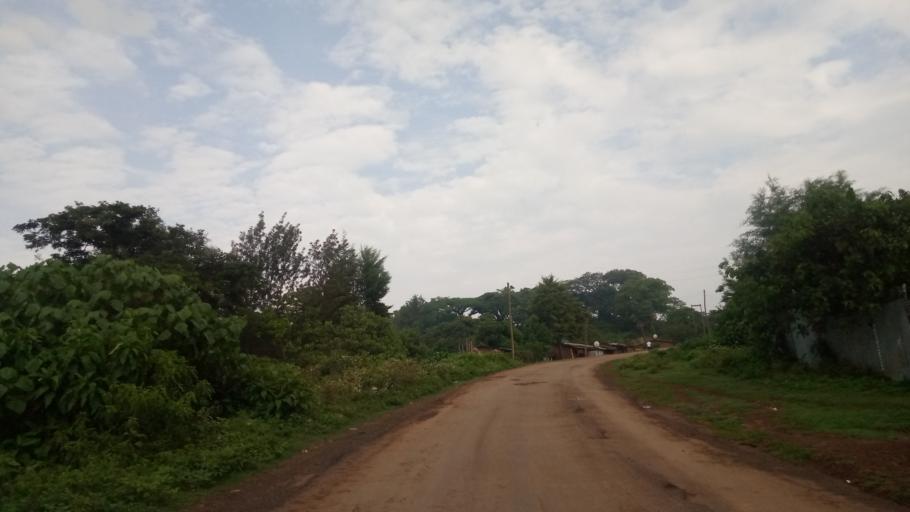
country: ET
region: Oromiya
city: Agaro
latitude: 7.8355
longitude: 36.6734
